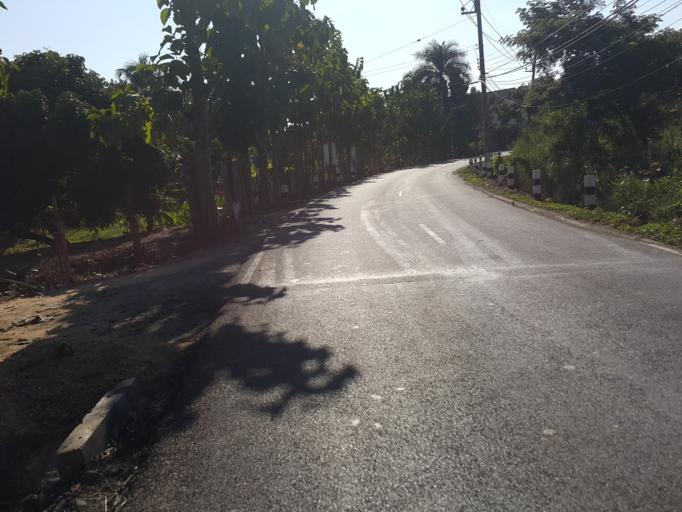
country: TH
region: Chiang Mai
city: San Kamphaeng
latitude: 18.7939
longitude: 99.1674
